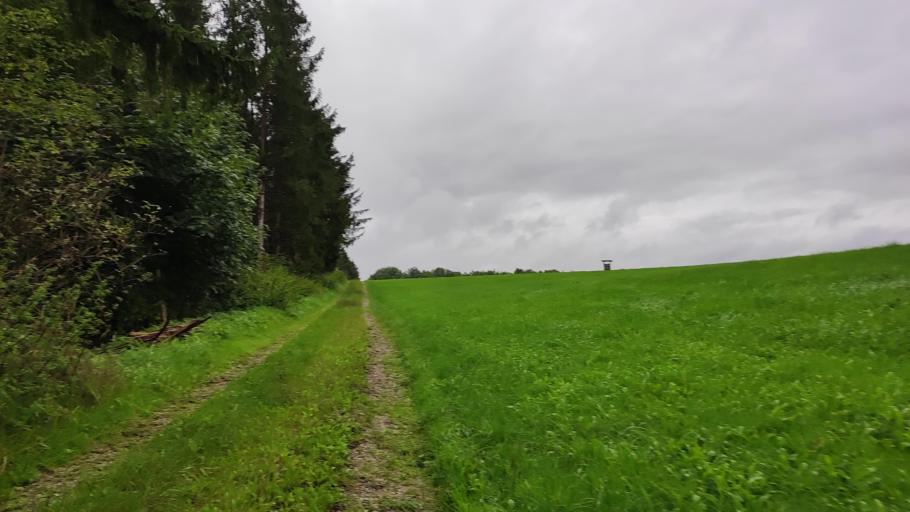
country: DE
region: Bavaria
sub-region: Swabia
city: Altenmunster
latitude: 48.4488
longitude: 10.6104
